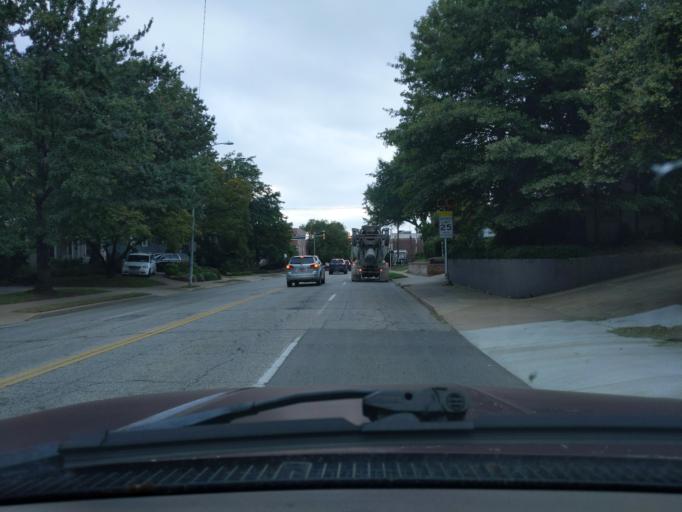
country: US
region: Oklahoma
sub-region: Tulsa County
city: Tulsa
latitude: 36.1334
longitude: -95.9823
